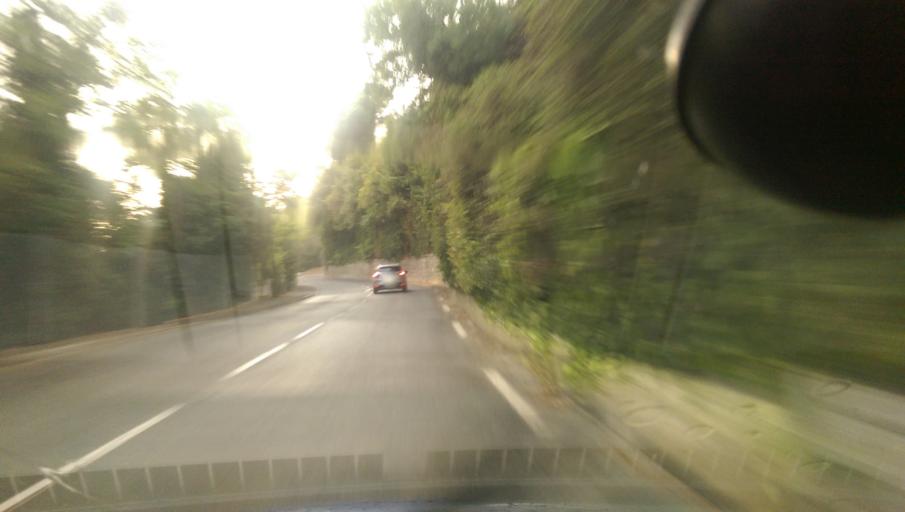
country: FR
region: Provence-Alpes-Cote d'Azur
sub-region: Departement des Alpes-Maritimes
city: Grasse
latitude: 43.6701
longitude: 6.9412
